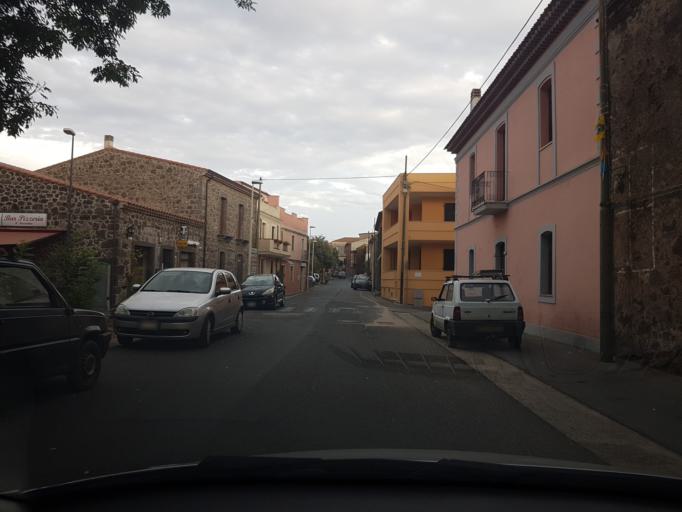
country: IT
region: Sardinia
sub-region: Provincia di Oristano
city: Seneghe
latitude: 40.0819
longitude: 8.6096
